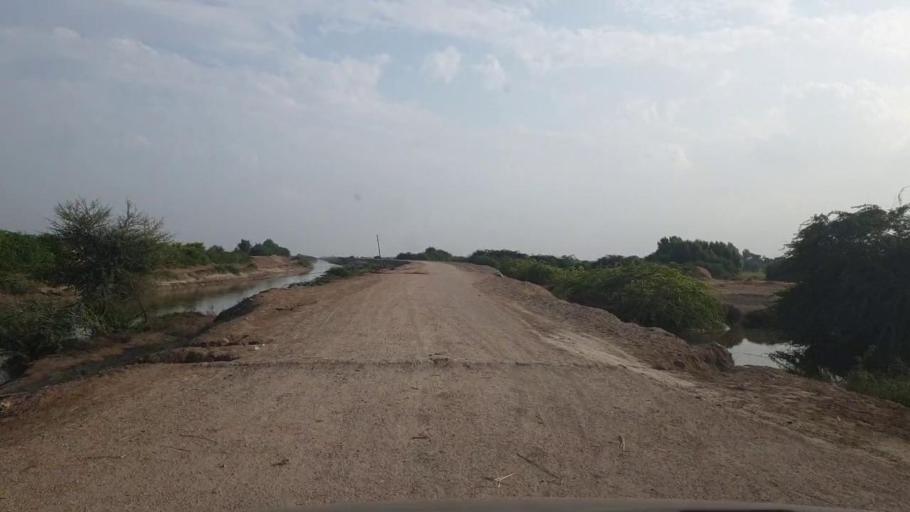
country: PK
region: Sindh
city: Badin
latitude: 24.5492
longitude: 68.6711
